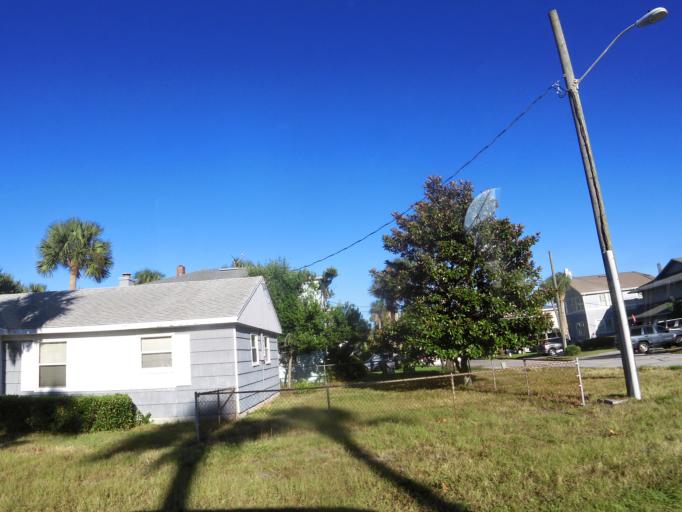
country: US
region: Florida
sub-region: Duval County
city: Neptune Beach
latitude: 30.3186
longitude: -81.3964
